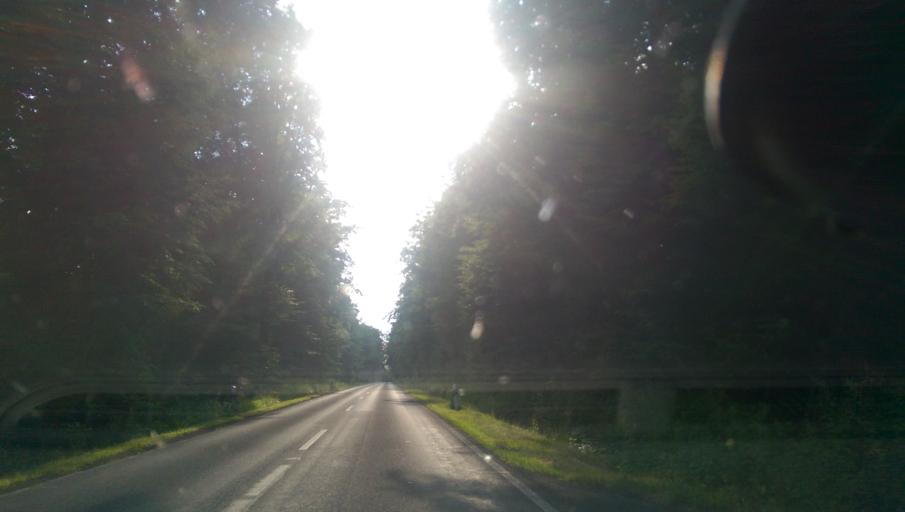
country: DE
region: Hesse
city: Herbstein
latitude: 50.5824
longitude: 9.3468
